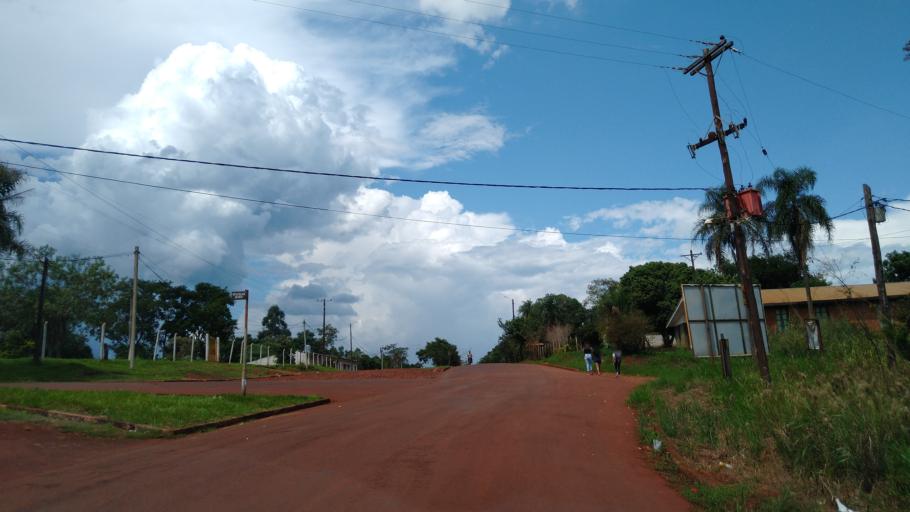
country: AR
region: Misiones
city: Puerto Libertad
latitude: -25.9666
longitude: -54.5937
